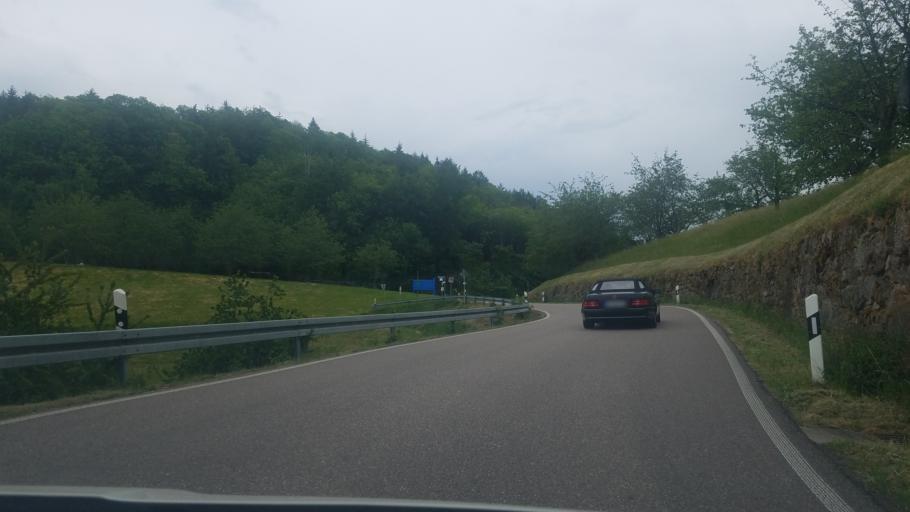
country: DE
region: Baden-Wuerttemberg
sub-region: Freiburg Region
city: Kappelrodeck
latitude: 48.6120
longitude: 8.1122
